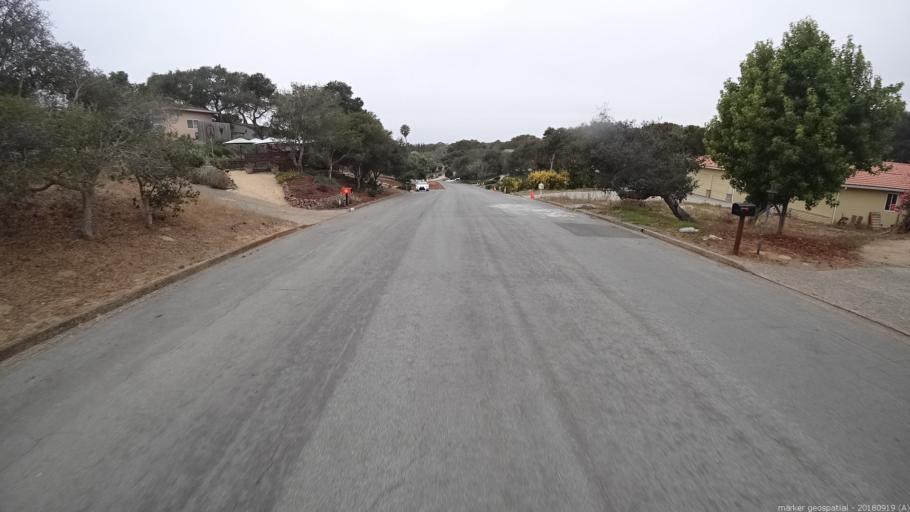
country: US
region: California
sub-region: Monterey County
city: Prunedale
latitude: 36.7804
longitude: -121.7103
